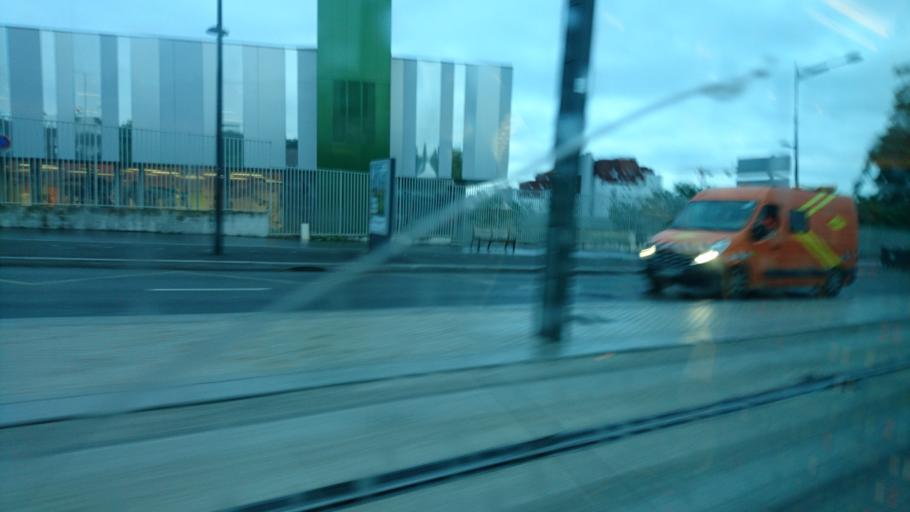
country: FR
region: Ile-de-France
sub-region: Departement de Seine-Saint-Denis
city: Pierrefitte-sur-Seine
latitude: 48.9733
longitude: 2.3661
